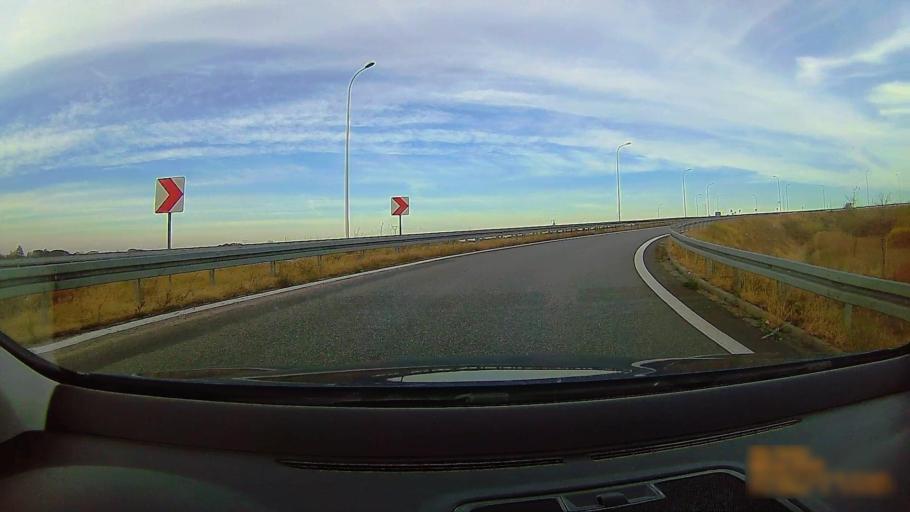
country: PL
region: Greater Poland Voivodeship
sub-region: Powiat ostrowski
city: Ostrow Wielkopolski
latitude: 51.6642
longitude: 17.8543
